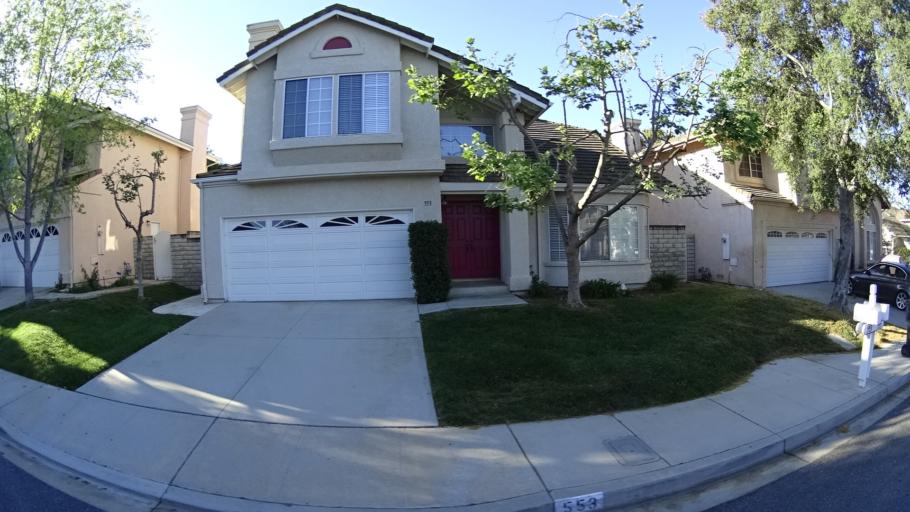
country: US
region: California
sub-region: Ventura County
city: Casa Conejo
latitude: 34.2175
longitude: -118.8903
